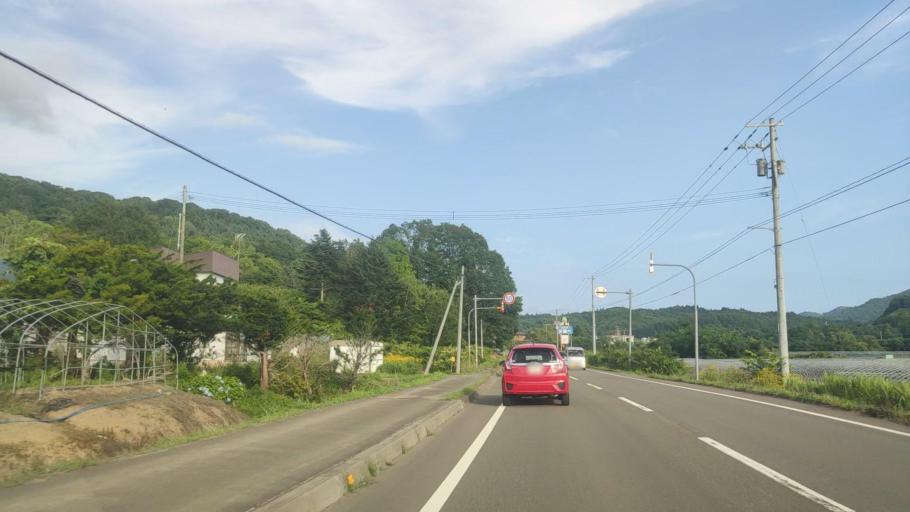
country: JP
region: Hokkaido
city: Iwamizawa
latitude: 43.0415
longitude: 141.9147
